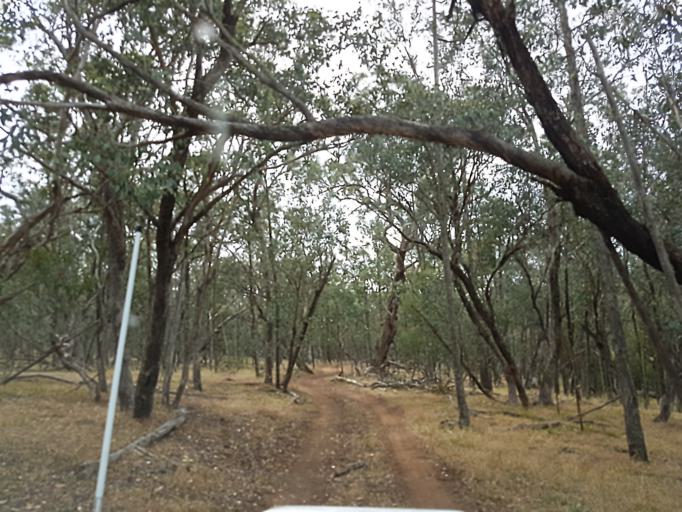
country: AU
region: New South Wales
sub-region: Snowy River
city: Jindabyne
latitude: -36.9581
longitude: 148.4096
